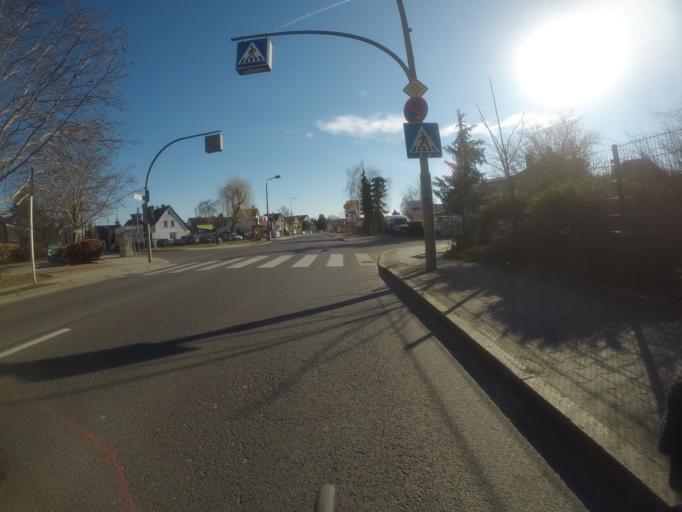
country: DE
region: Berlin
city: Kopenick Bezirk
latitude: 52.4709
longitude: 13.5724
